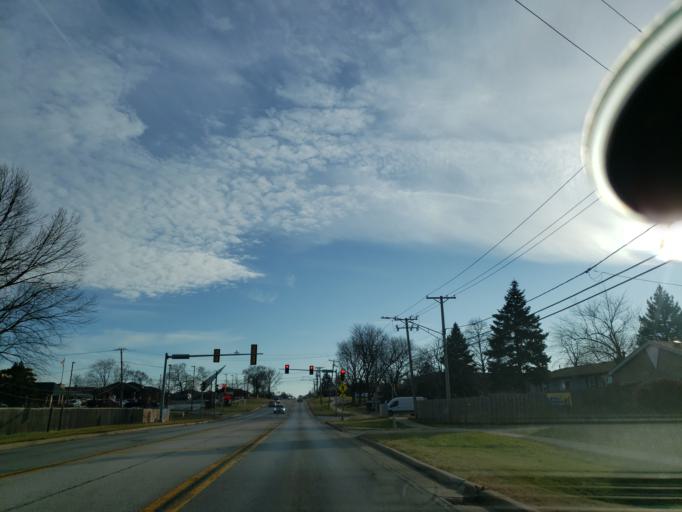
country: US
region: Illinois
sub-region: Cook County
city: Oak Forest
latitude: 41.6086
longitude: -87.7562
